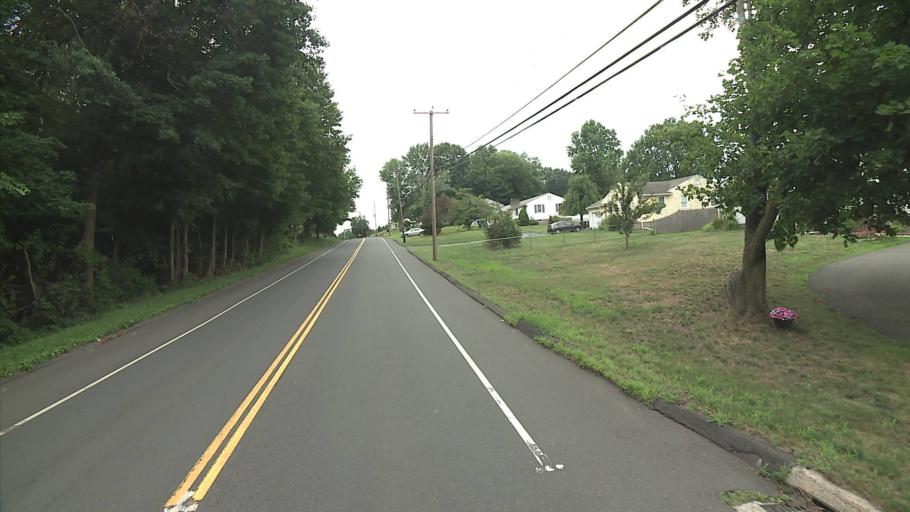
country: US
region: Connecticut
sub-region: Middlesex County
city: Cromwell
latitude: 41.6497
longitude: -72.6434
